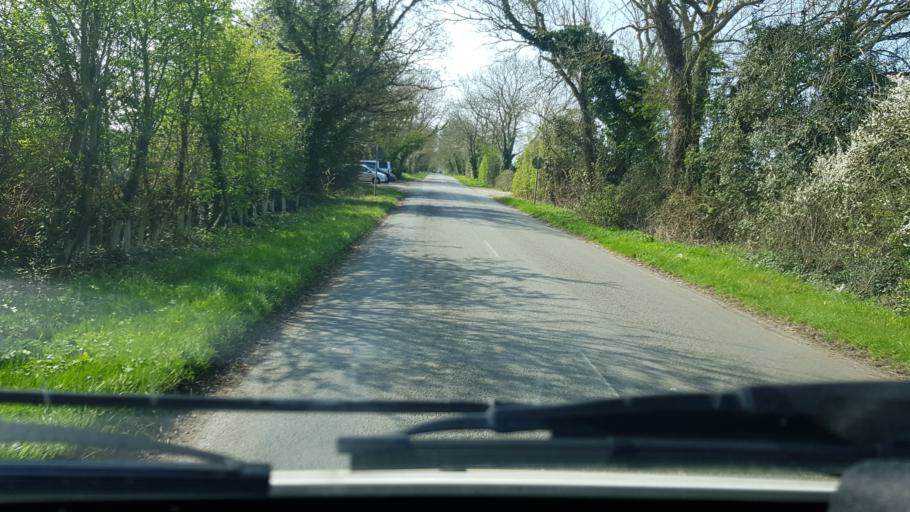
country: GB
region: England
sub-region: West Sussex
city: Chichester
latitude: 50.8625
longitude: -0.7889
